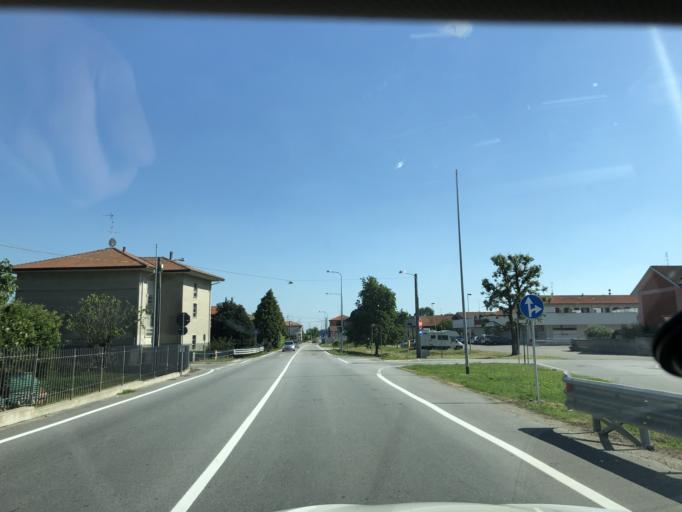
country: IT
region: Piedmont
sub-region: Provincia di Novara
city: Oleggio
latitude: 45.5987
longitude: 8.6447
